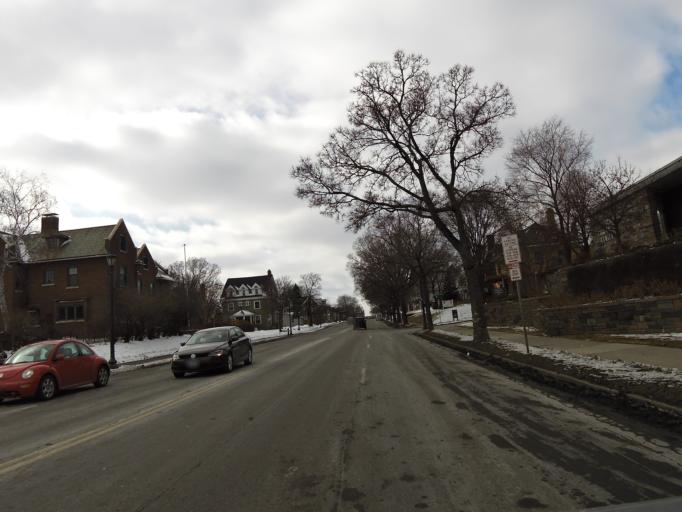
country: US
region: Minnesota
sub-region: Hennepin County
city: Minneapolis
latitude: 44.9627
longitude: -93.2802
